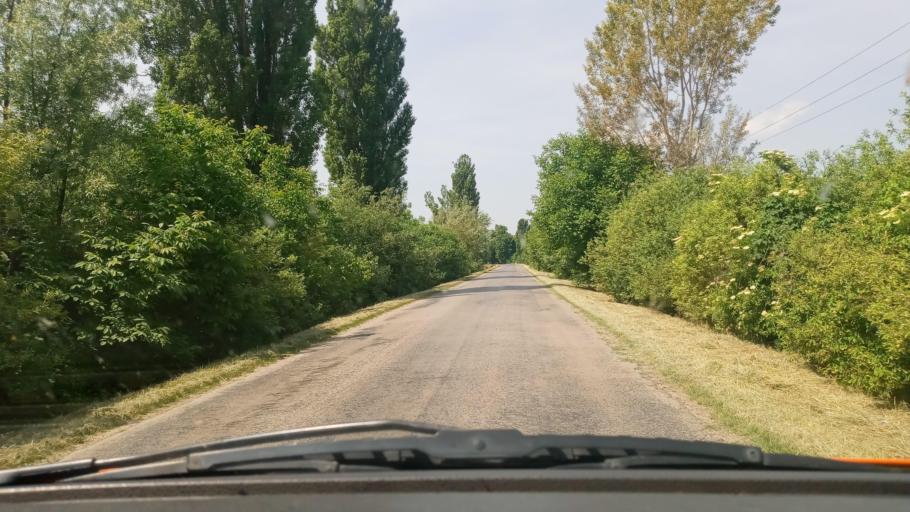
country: HU
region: Baranya
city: Szigetvar
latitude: 45.9662
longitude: 17.6887
